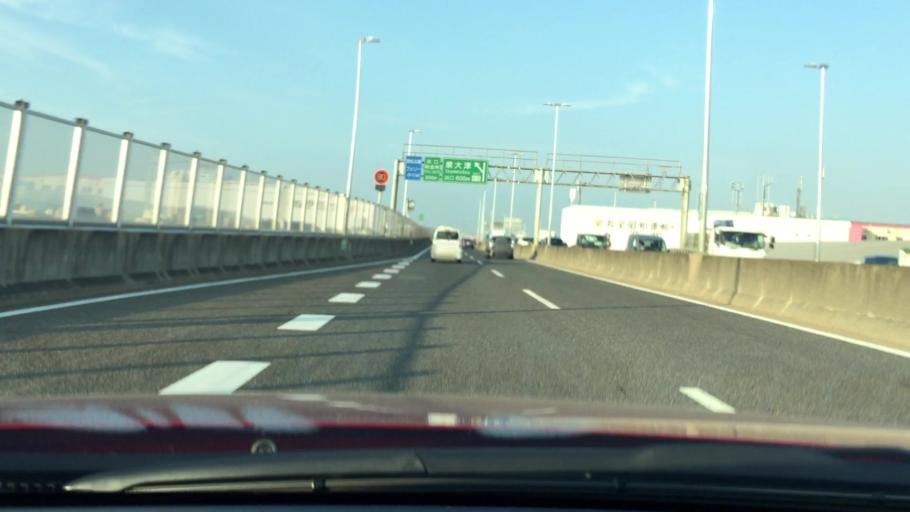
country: JP
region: Osaka
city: Takaishi
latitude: 34.5158
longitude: 135.4153
